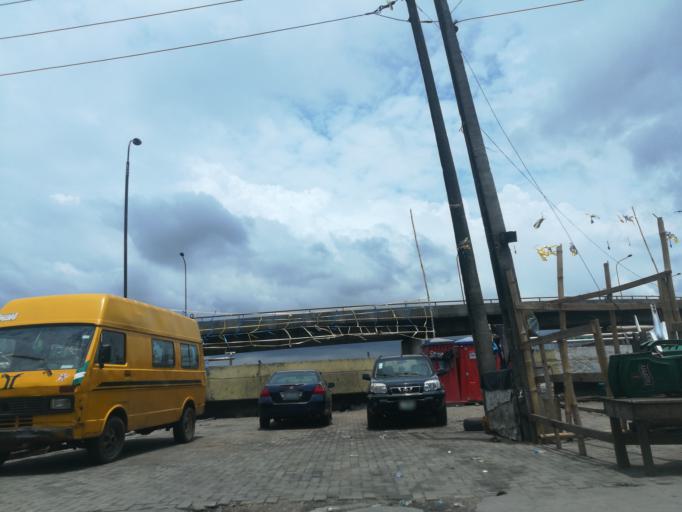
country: NG
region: Lagos
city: Lagos
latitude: 6.4638
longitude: 3.3854
